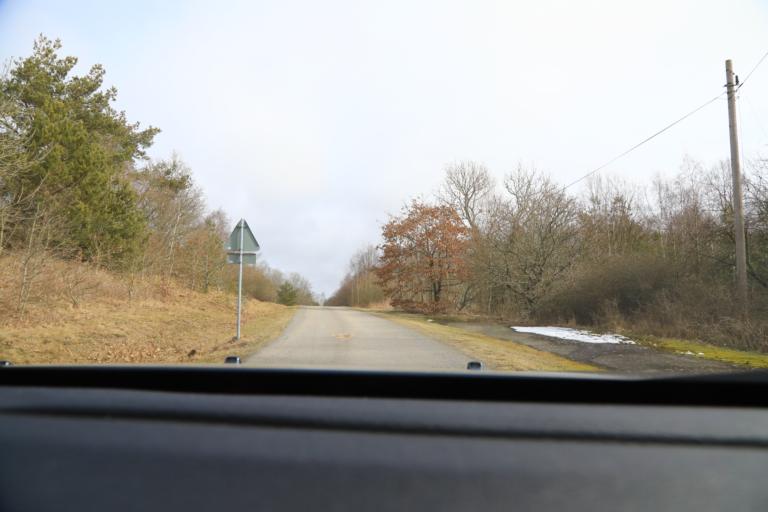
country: SE
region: Halland
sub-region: Varbergs Kommun
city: Varberg
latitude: 57.2046
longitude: 12.2333
